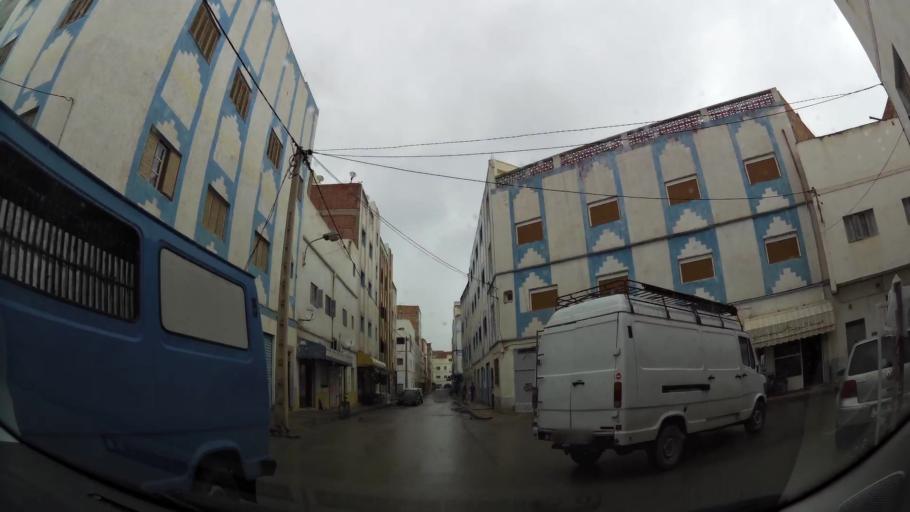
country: MA
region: Taza-Al Hoceima-Taounate
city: Imzourene
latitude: 35.1441
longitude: -3.8511
